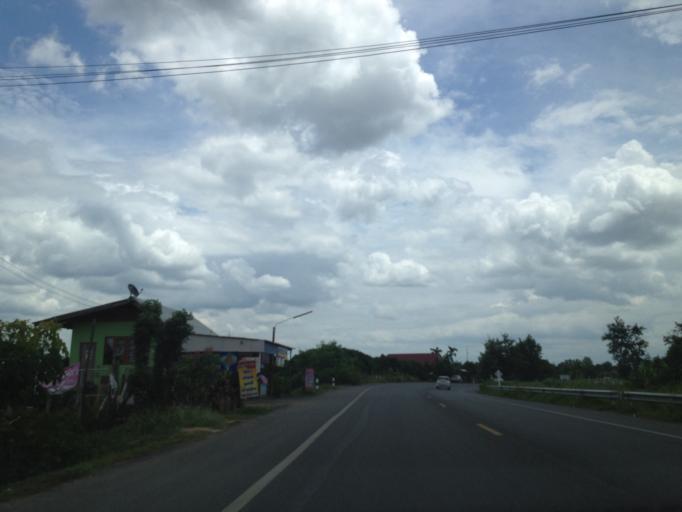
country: TH
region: Chiang Mai
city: San Pa Tong
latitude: 18.6333
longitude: 98.8772
